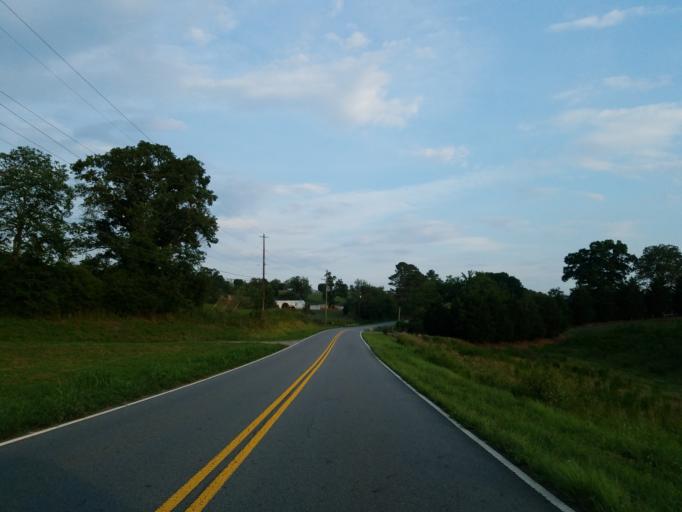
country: US
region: Georgia
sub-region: Gilmer County
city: Ellijay
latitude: 34.6531
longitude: -84.4706
